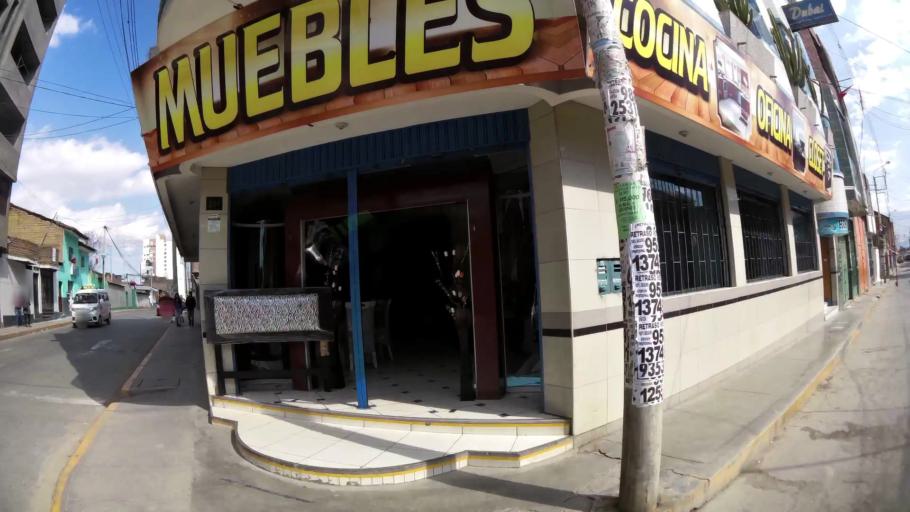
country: PE
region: Junin
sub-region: Provincia de Huancayo
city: El Tambo
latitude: -12.0731
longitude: -75.2109
